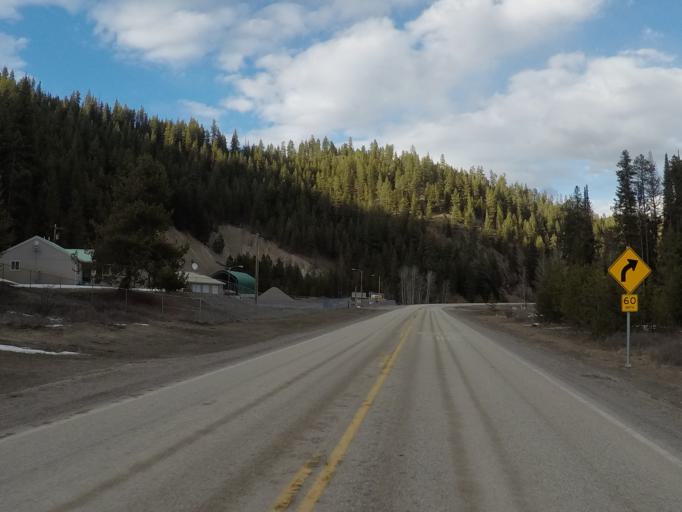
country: US
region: Montana
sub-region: Missoula County
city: Frenchtown
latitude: 46.7499
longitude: -114.5145
